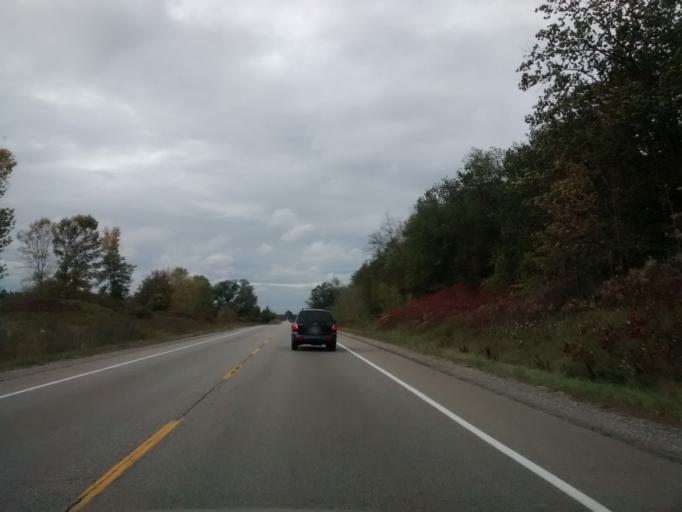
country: CA
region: Ontario
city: Ancaster
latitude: 43.0707
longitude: -79.9760
